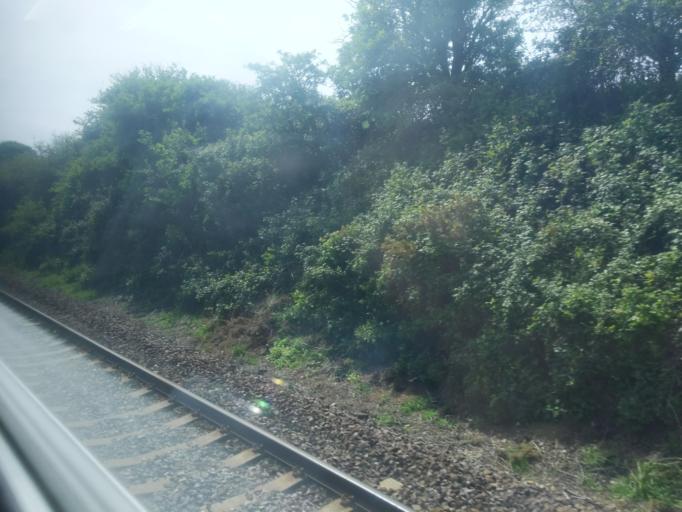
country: GB
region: England
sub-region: Cornwall
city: Hayle
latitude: 50.1630
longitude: -5.4527
